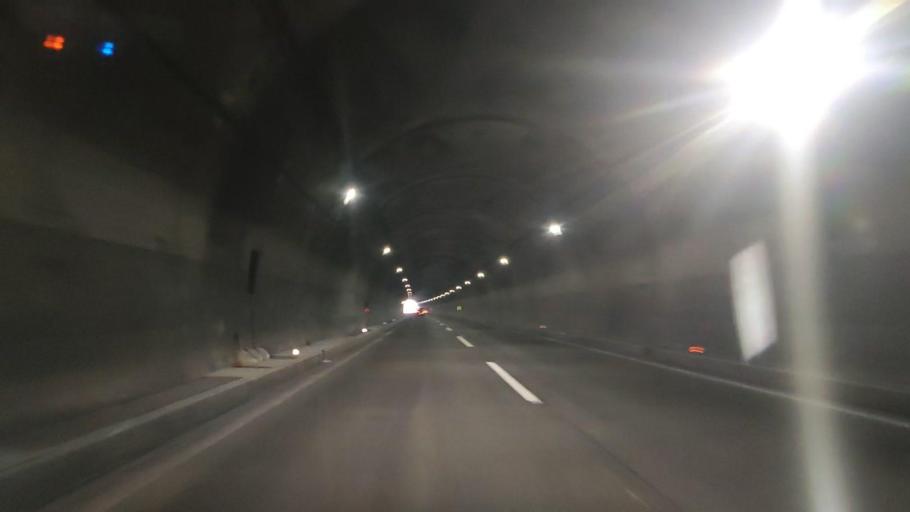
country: JP
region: Oita
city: Beppu
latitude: 33.2752
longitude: 131.3433
